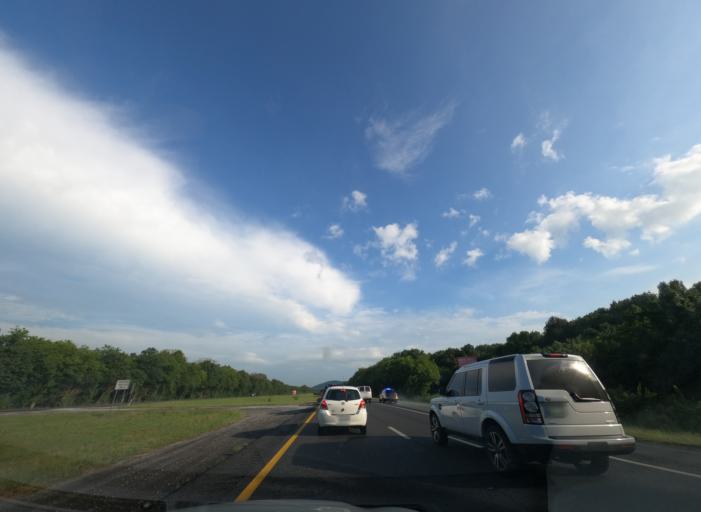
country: US
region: Tennessee
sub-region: Rutherford County
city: Plainview
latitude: 35.6760
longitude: -86.2849
